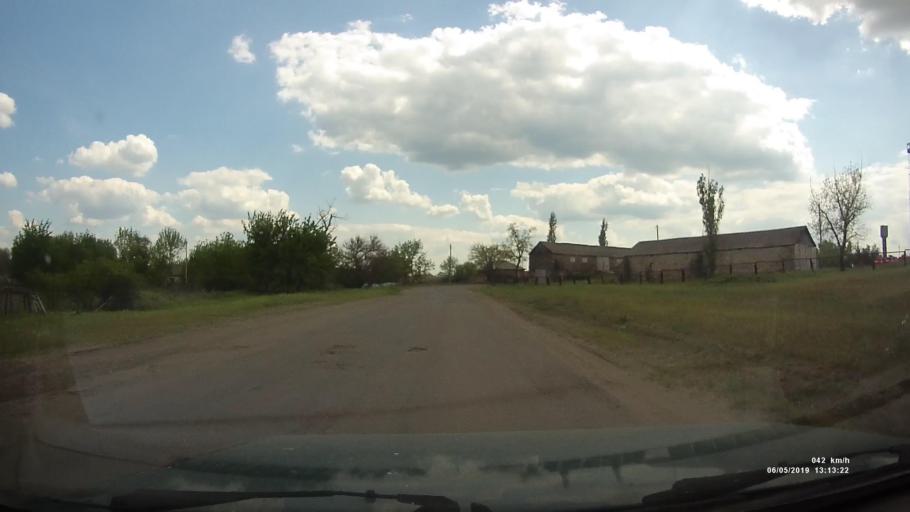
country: RU
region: Rostov
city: Ust'-Donetskiy
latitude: 47.7536
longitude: 40.9391
